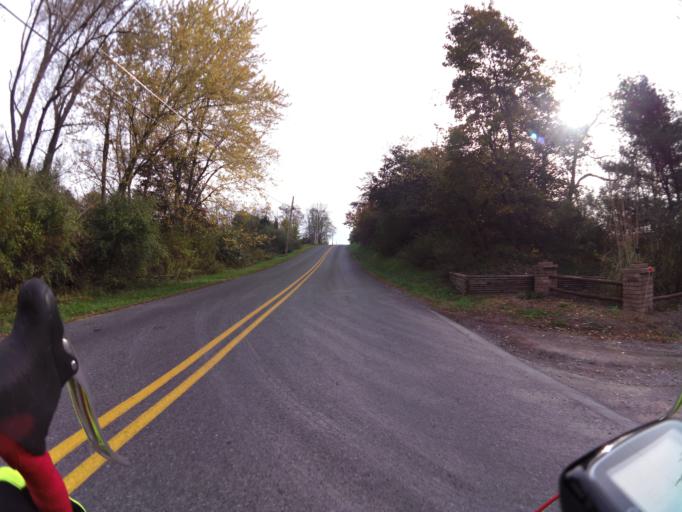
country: US
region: Pennsylvania
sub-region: Union County
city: New Columbia
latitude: 41.0454
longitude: -76.8899
